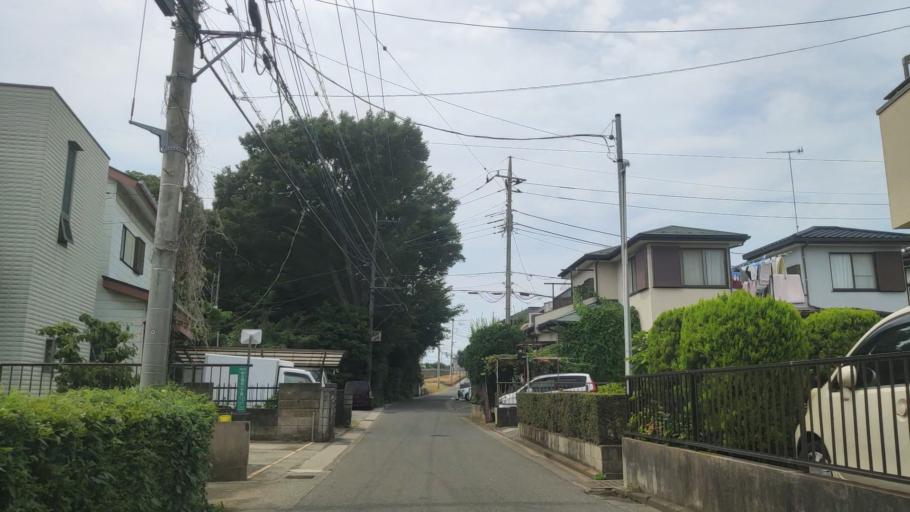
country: JP
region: Kanagawa
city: Atsugi
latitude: 35.4303
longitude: 139.3964
